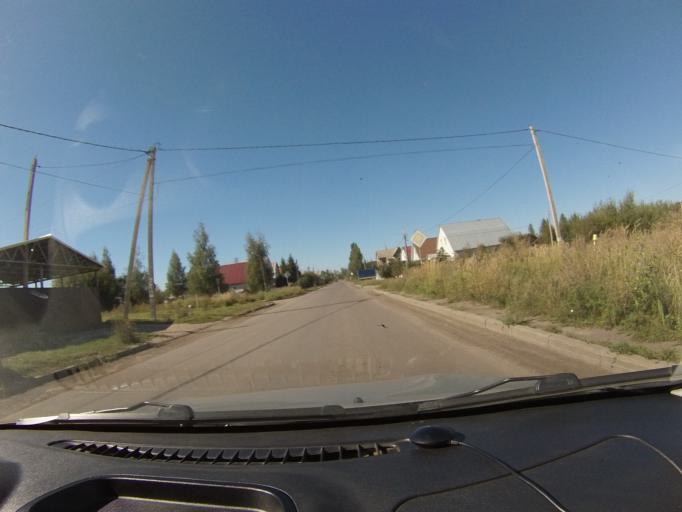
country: RU
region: Tambov
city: Tambov
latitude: 52.7652
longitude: 41.3686
